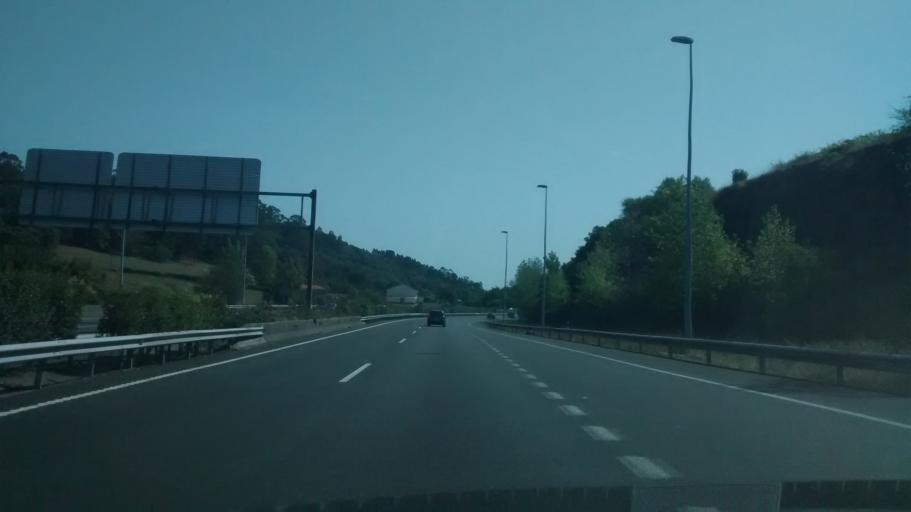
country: ES
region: Cantabria
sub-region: Provincia de Cantabria
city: Barcena de Cicero
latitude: 43.4133
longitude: -3.5392
